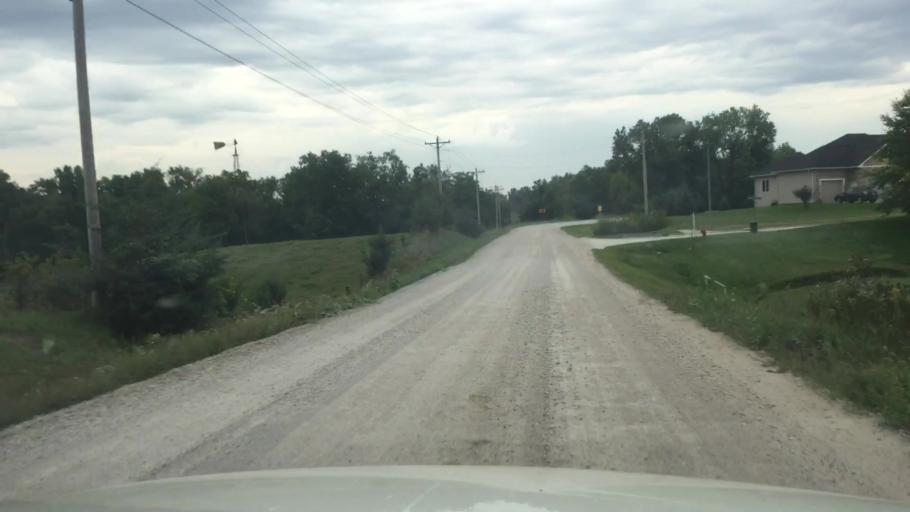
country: US
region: Iowa
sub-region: Story County
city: Huxley
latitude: 41.8948
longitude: -93.5810
